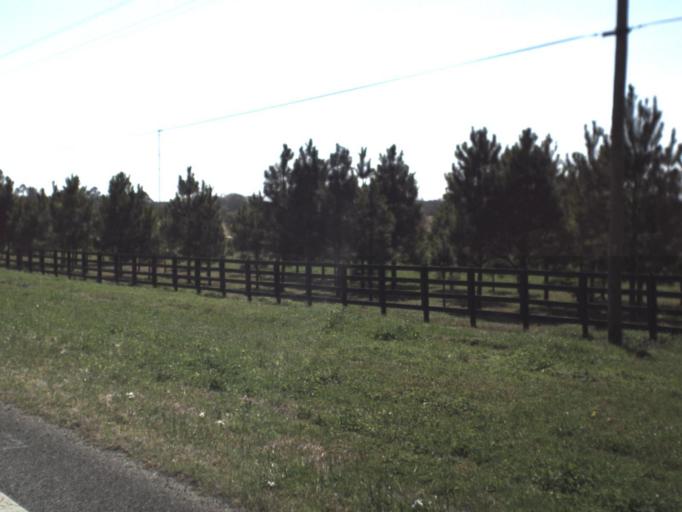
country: US
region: Florida
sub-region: Jackson County
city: Graceville
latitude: 30.9181
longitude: -85.3817
